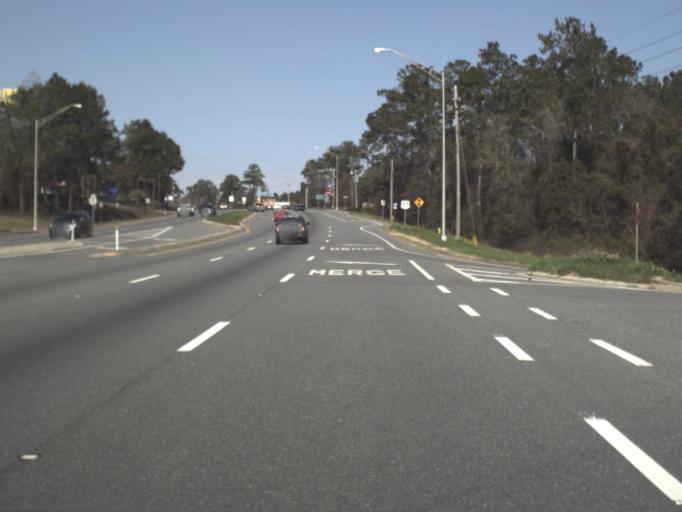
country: US
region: Florida
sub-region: Leon County
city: Tallahassee
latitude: 30.4851
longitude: -84.3130
